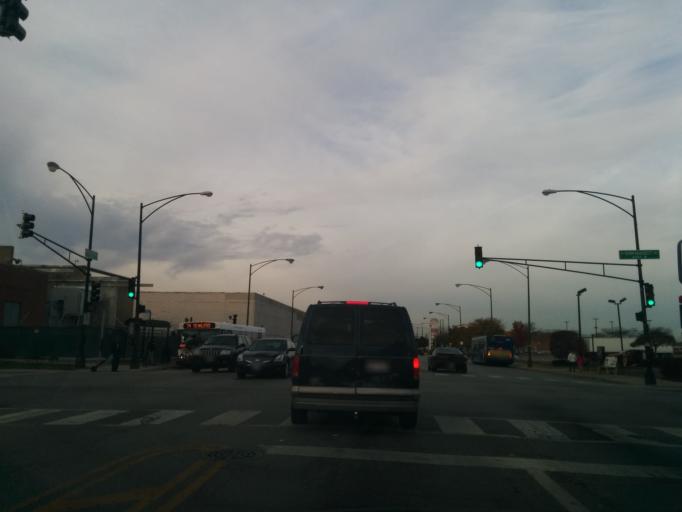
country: US
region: Illinois
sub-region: Cook County
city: Elmwood Park
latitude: 41.9237
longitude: -87.7852
